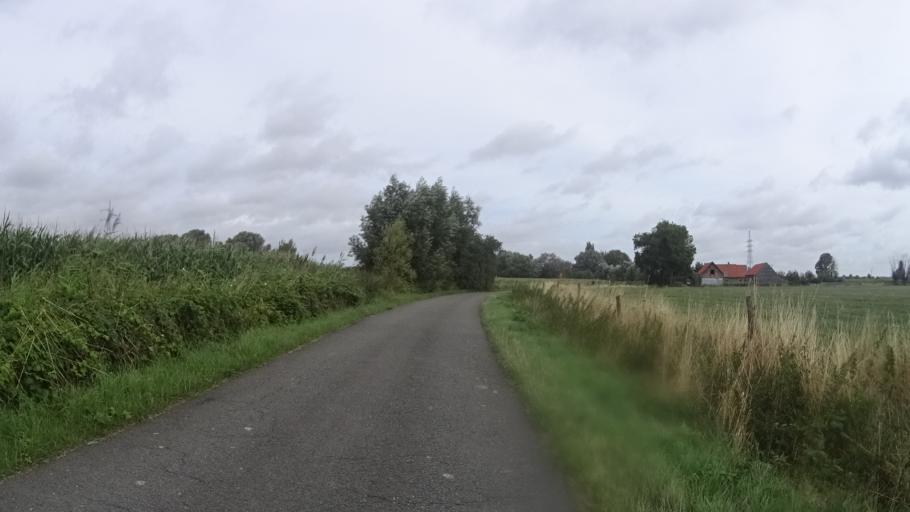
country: BE
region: Flanders
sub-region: Provincie West-Vlaanderen
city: Diksmuide
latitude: 51.0483
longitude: 2.8911
